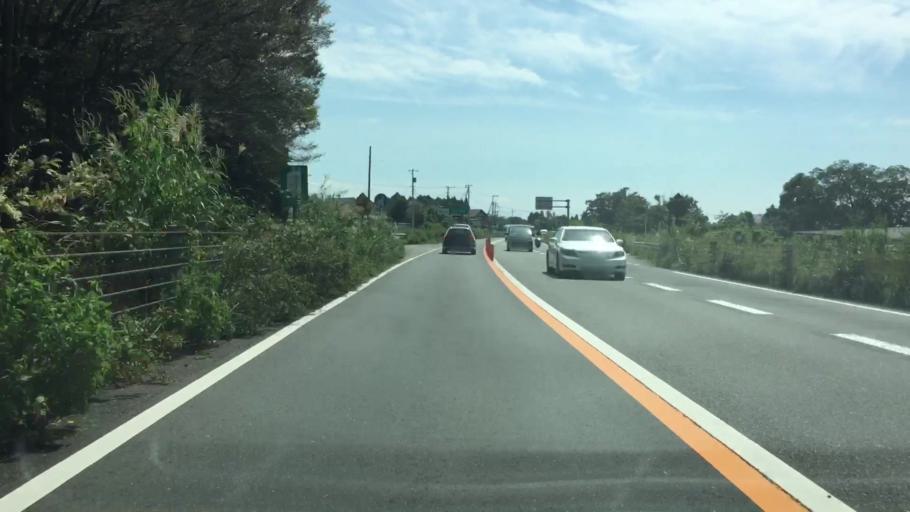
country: JP
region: Shizuoka
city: Fujinomiya
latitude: 35.2865
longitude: 138.6119
